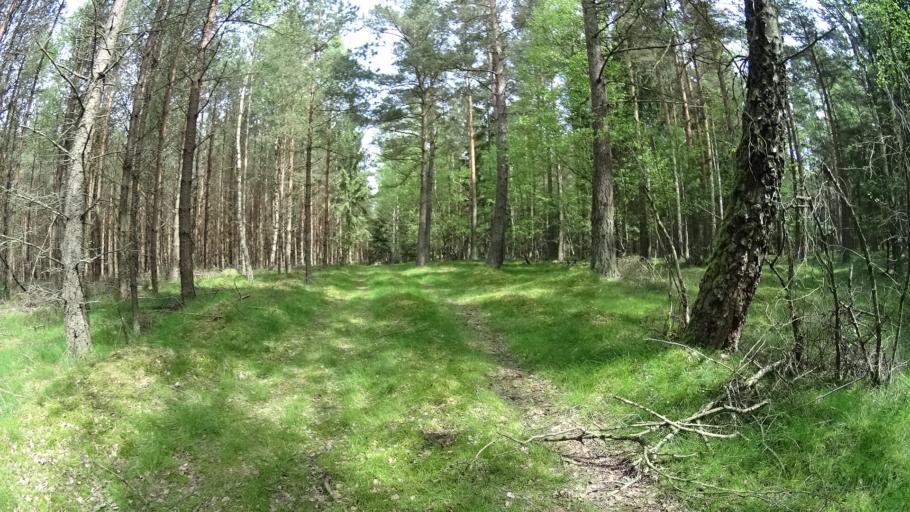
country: SE
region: Skane
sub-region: Sjobo Kommun
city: Sjoebo
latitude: 55.6715
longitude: 13.6367
